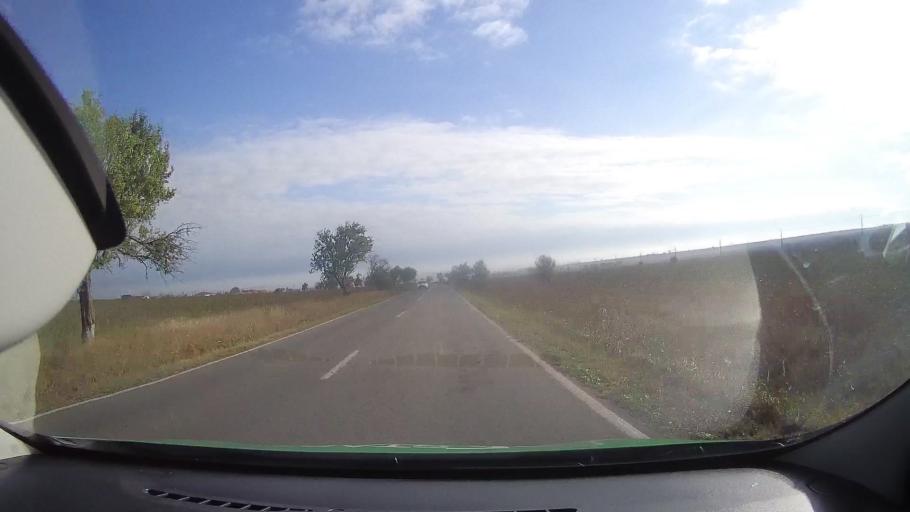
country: RO
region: Tulcea
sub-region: Comuna Mahmudia
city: Mahmudia
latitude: 45.0774
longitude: 29.0714
